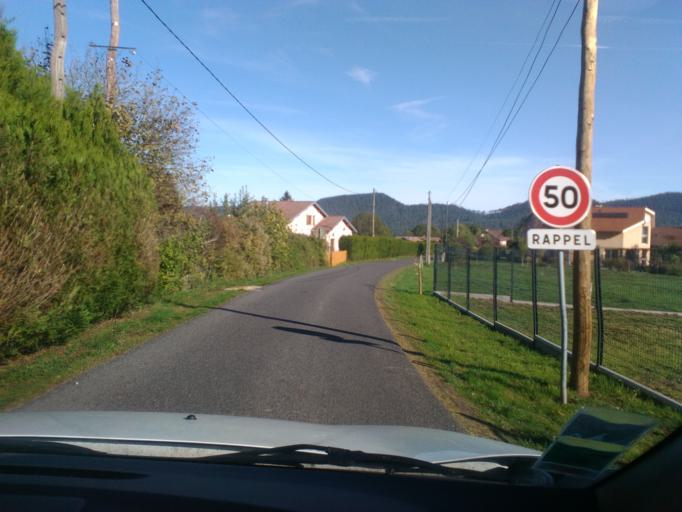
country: FR
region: Lorraine
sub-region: Departement des Vosges
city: Taintrux
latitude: 48.2357
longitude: 6.8837
